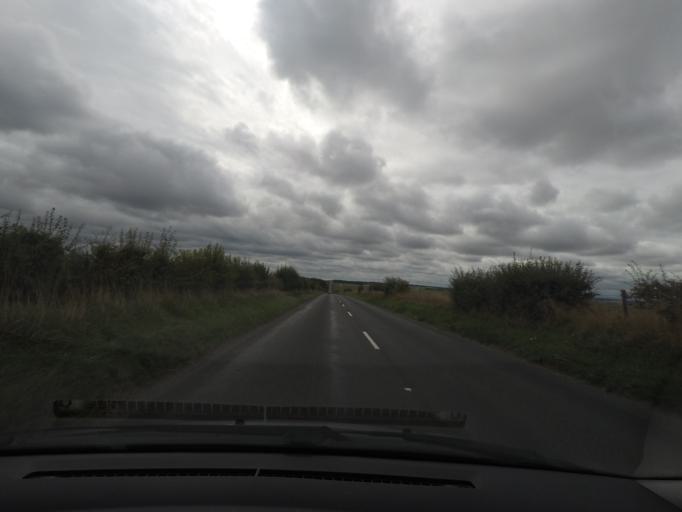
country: GB
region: England
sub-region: Wiltshire
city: Shrewton
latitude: 51.1975
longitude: -1.8622
